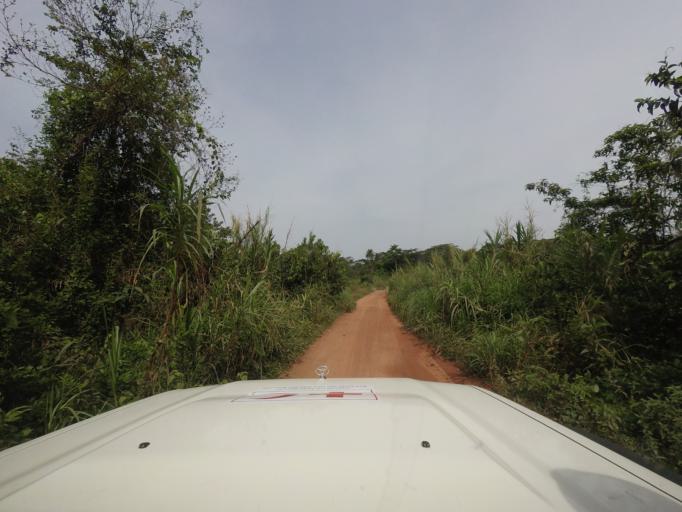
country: GN
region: Nzerekore
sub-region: Macenta
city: Macenta
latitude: 8.4745
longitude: -9.5620
